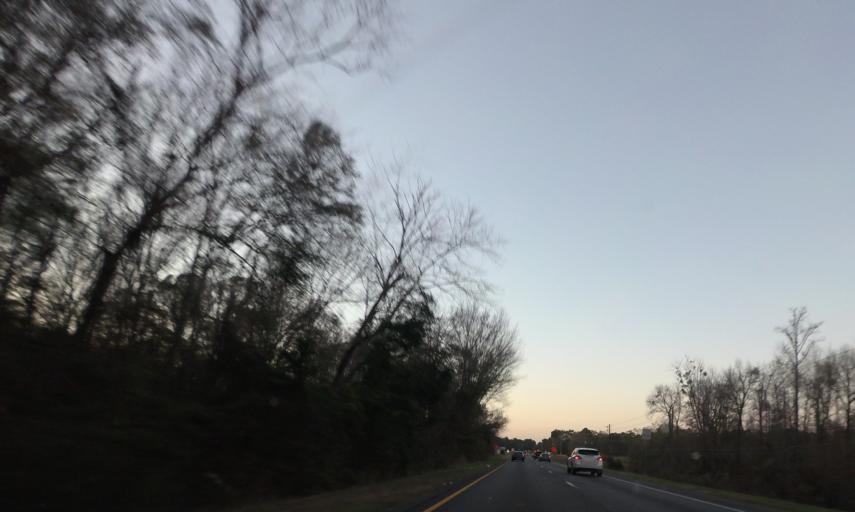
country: US
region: Georgia
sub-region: Houston County
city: Warner Robins
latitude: 32.6695
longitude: -83.6220
